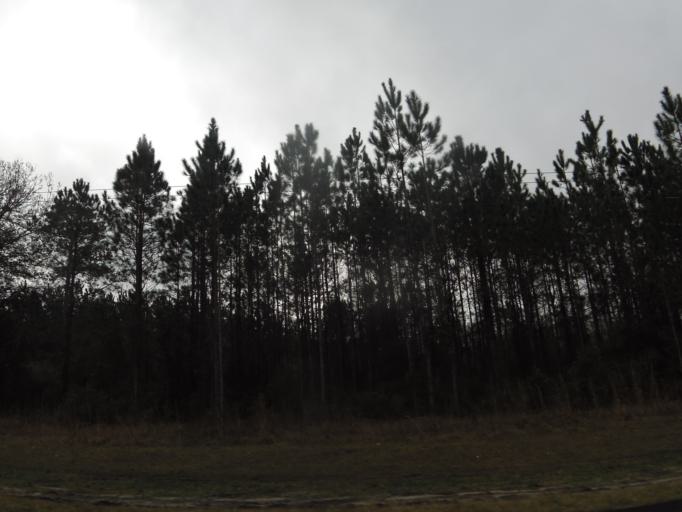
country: US
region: Florida
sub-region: Gilchrist County
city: Trenton
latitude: 29.7916
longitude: -82.8052
